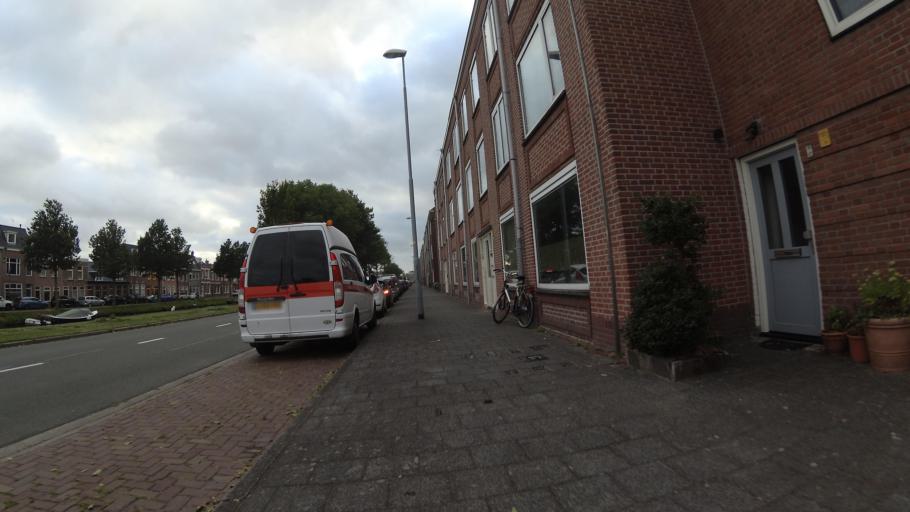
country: NL
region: North Holland
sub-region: Gemeente Den Helder
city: Den Helder
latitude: 52.9630
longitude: 4.7588
